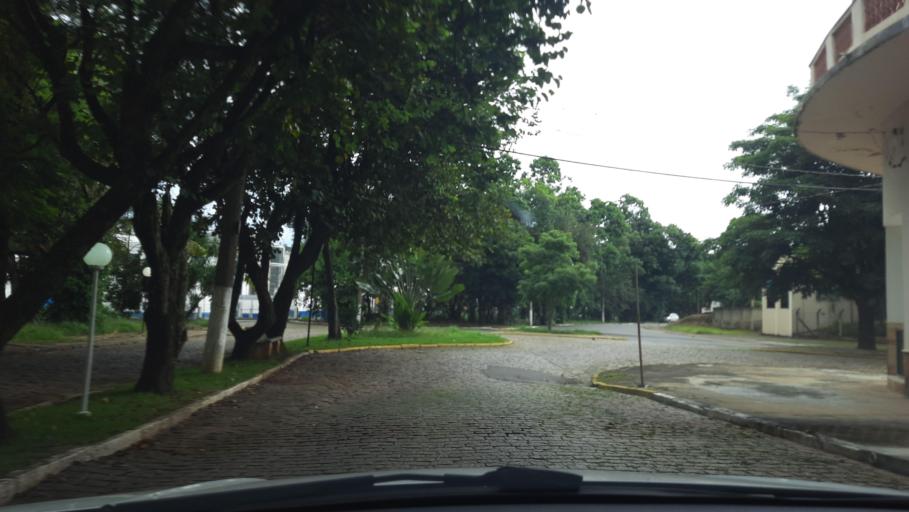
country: BR
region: Sao Paulo
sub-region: Sao Joao Da Boa Vista
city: Sao Joao da Boa Vista
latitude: -21.9391
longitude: -46.7160
